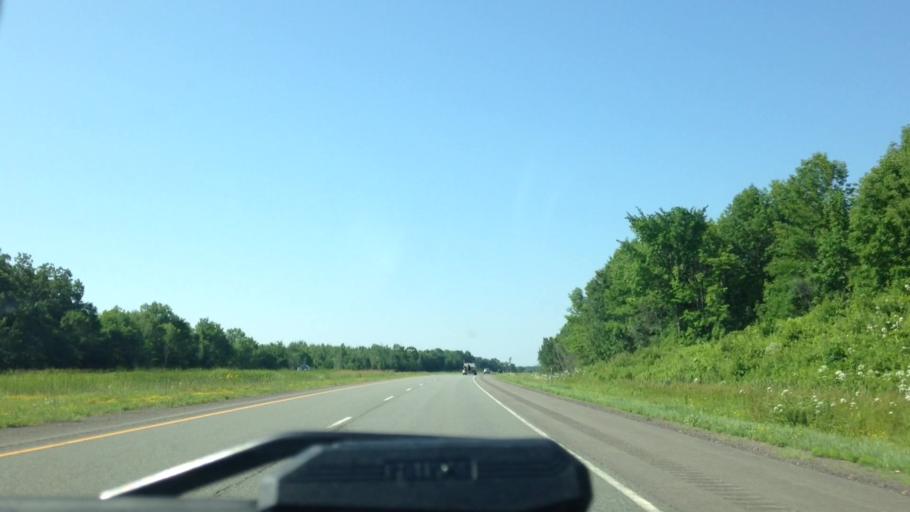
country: US
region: Wisconsin
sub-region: Douglas County
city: Lake Nebagamon
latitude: 46.4117
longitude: -91.8111
